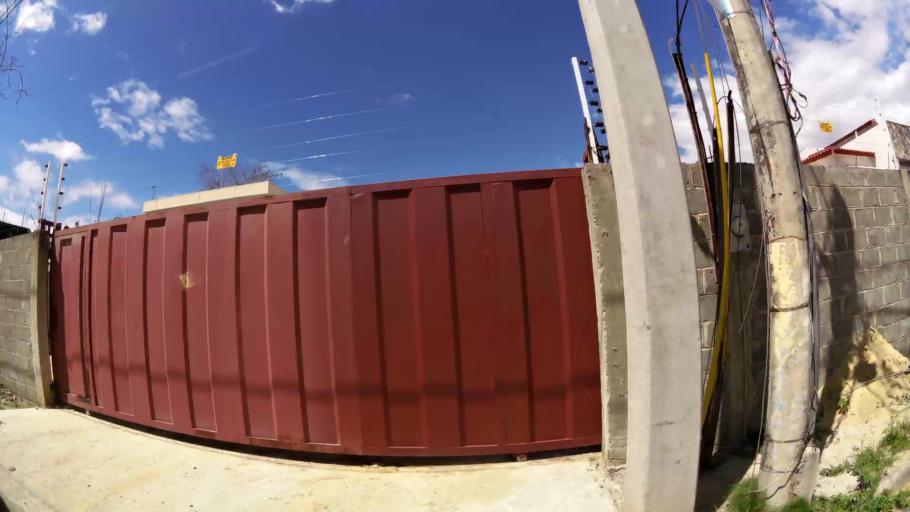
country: DO
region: San Cristobal
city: San Cristobal
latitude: 18.4171
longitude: -70.0913
